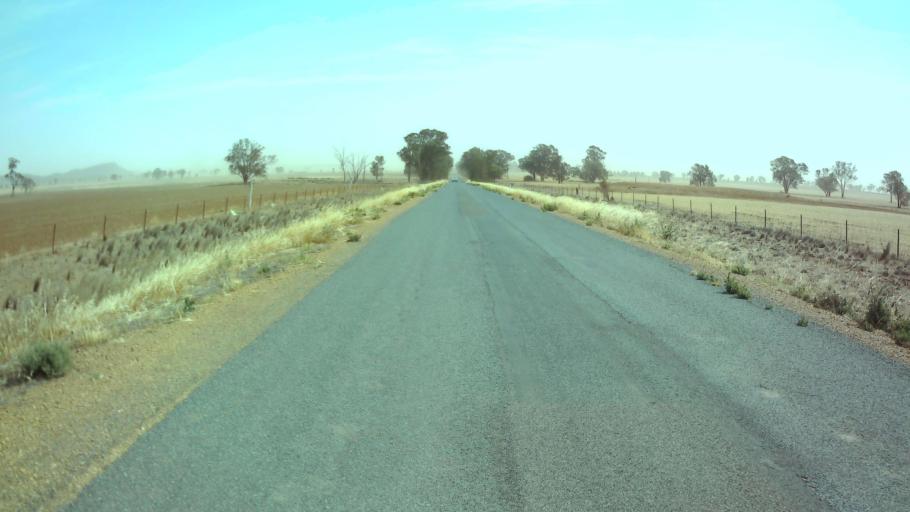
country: AU
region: New South Wales
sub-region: Weddin
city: Grenfell
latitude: -33.7646
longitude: 147.9881
